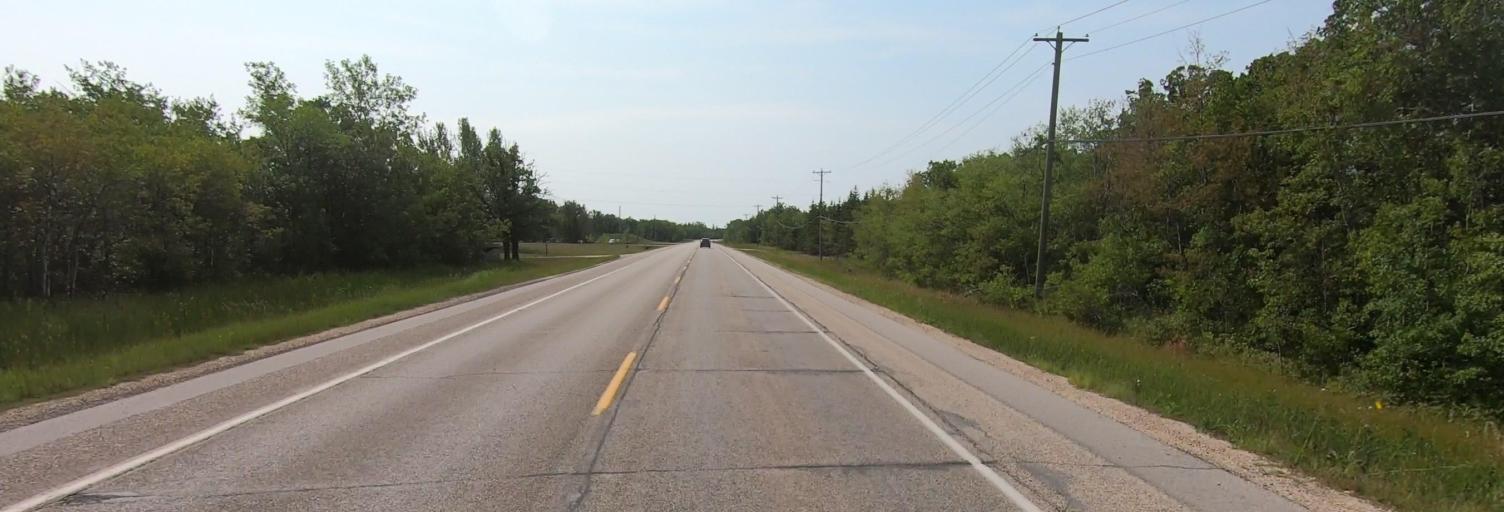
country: CA
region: Manitoba
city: Niverville
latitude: 49.7223
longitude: -97.0909
